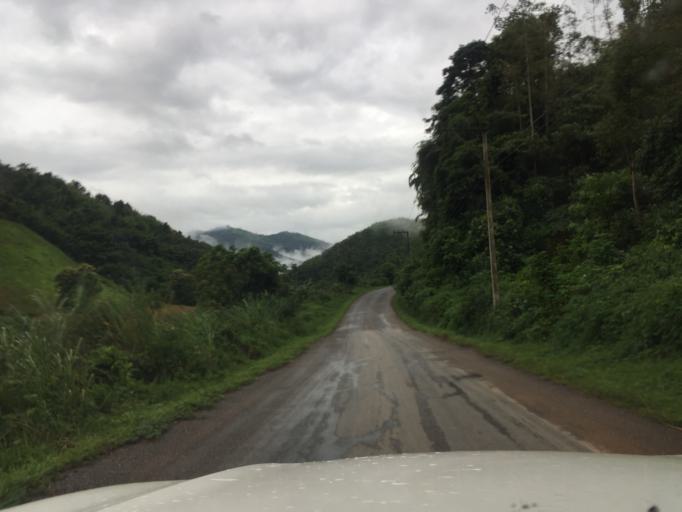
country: LA
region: Oudomxai
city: Muang La
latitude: 20.9472
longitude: 102.2097
